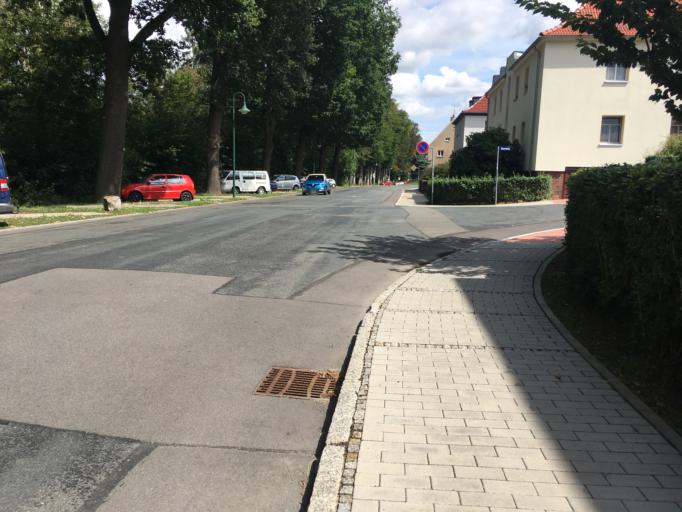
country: DE
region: Saxony
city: Crimmitschau
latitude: 50.8269
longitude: 12.3815
